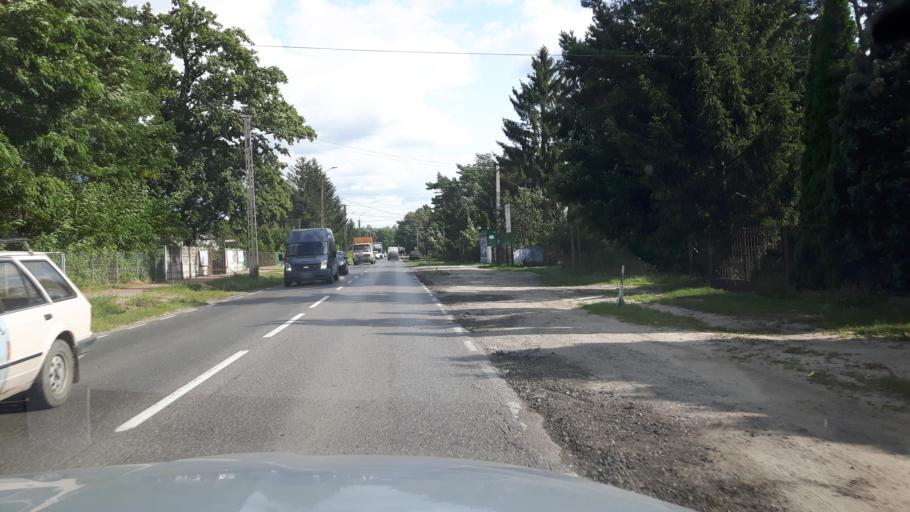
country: PL
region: Masovian Voivodeship
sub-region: Powiat wolominski
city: Radzymin
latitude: 52.3888
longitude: 21.2042
